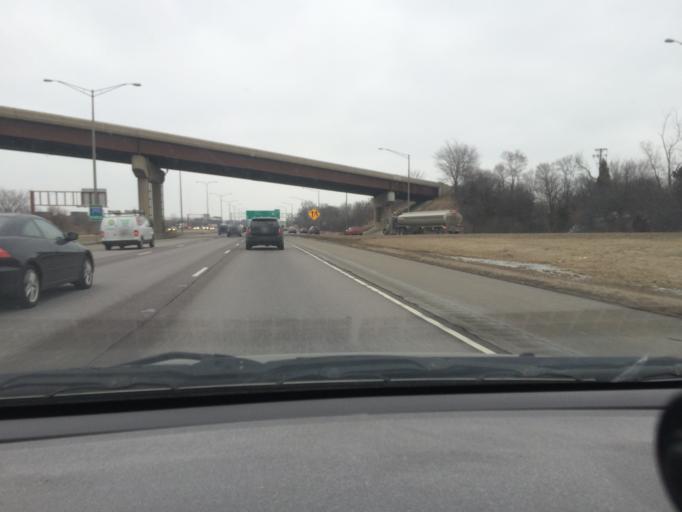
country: US
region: Illinois
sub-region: DuPage County
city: Itasca
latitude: 41.9607
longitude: -88.0260
